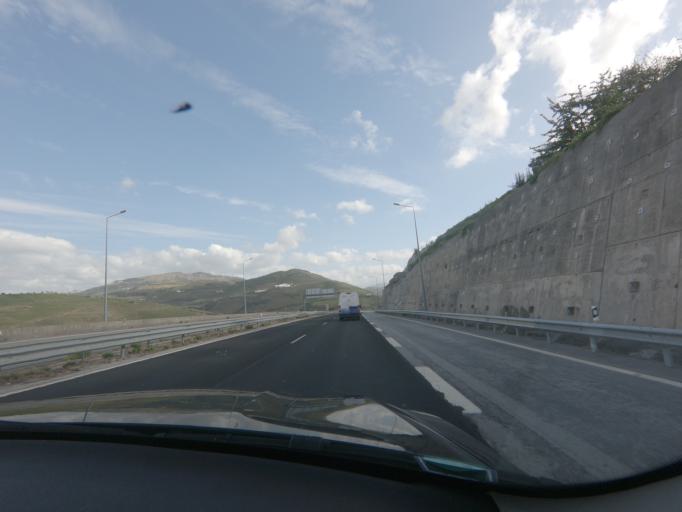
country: PT
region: Vila Real
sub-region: Peso da Regua
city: Peso da Regua
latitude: 41.1651
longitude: -7.7713
